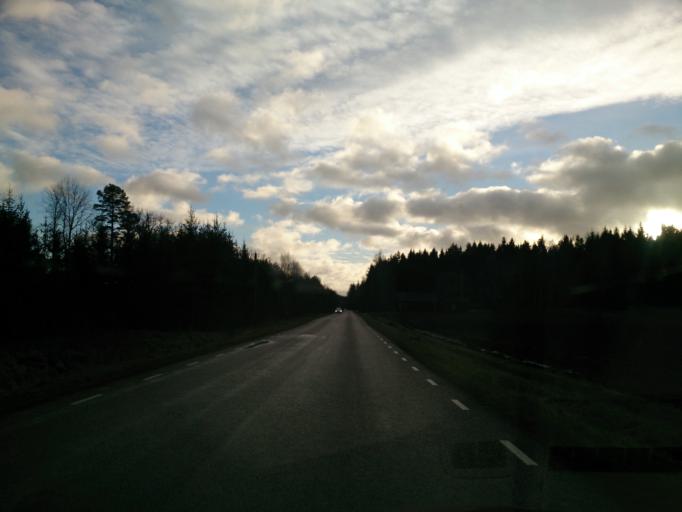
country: SE
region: OEstergoetland
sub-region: Atvidabergs Kommun
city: Atvidaberg
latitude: 58.3260
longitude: 16.0260
